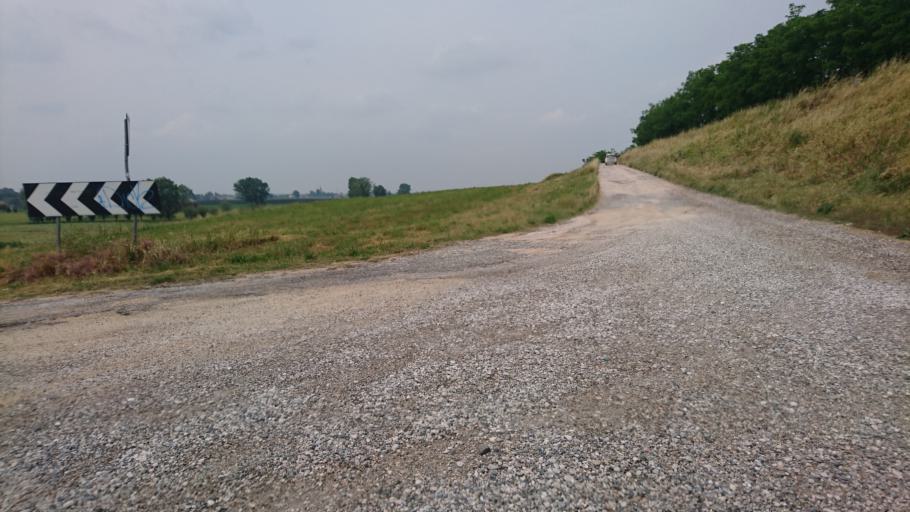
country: IT
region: Veneto
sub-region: Provincia di Rovigo
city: Lendinara
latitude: 45.1082
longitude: 11.6154
